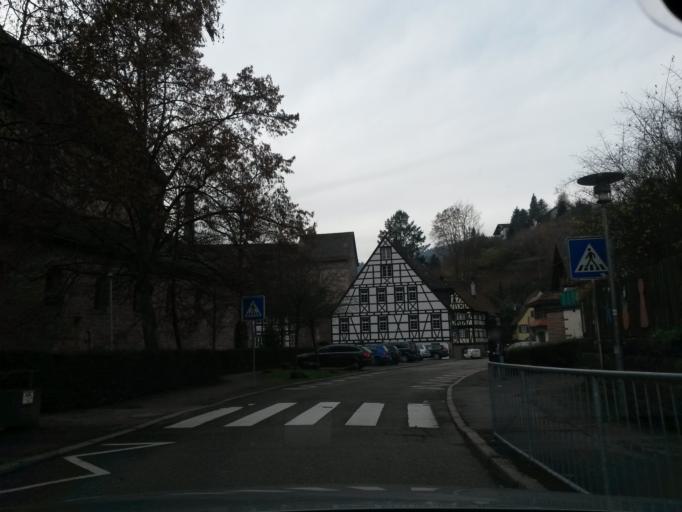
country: DE
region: Baden-Wuerttemberg
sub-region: Karlsruhe Region
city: Alpirsbach
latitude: 48.3468
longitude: 8.4043
